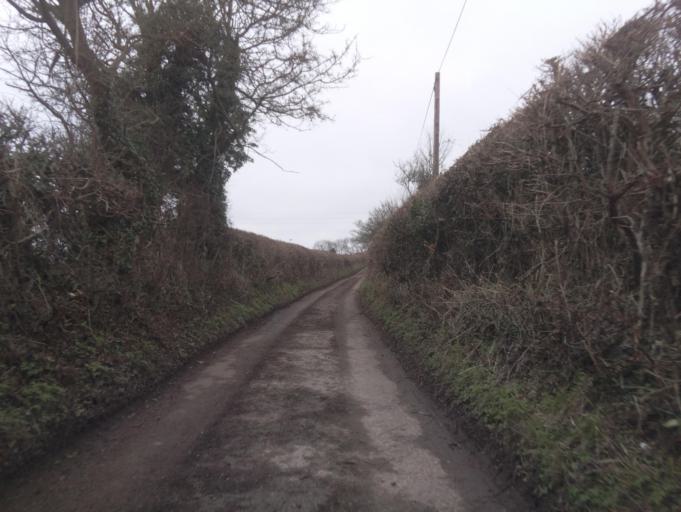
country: GB
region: England
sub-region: Wiltshire
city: Biddestone
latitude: 51.4658
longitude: -2.2333
